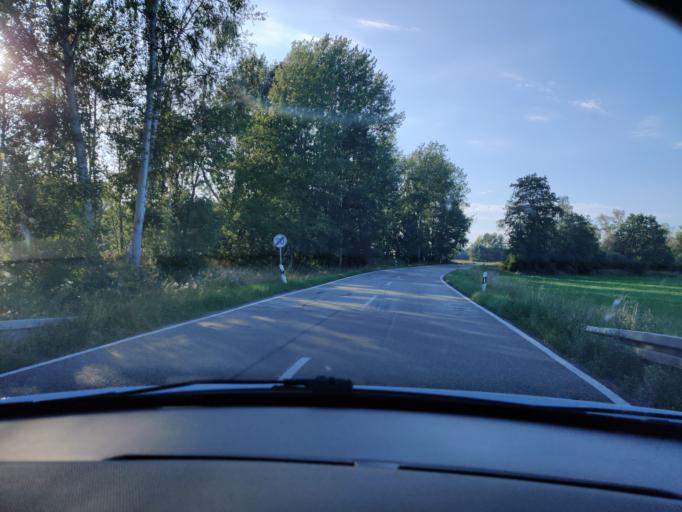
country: DE
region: Bavaria
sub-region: Upper Palatinate
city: Schwarzenfeld
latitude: 49.4006
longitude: 12.1326
